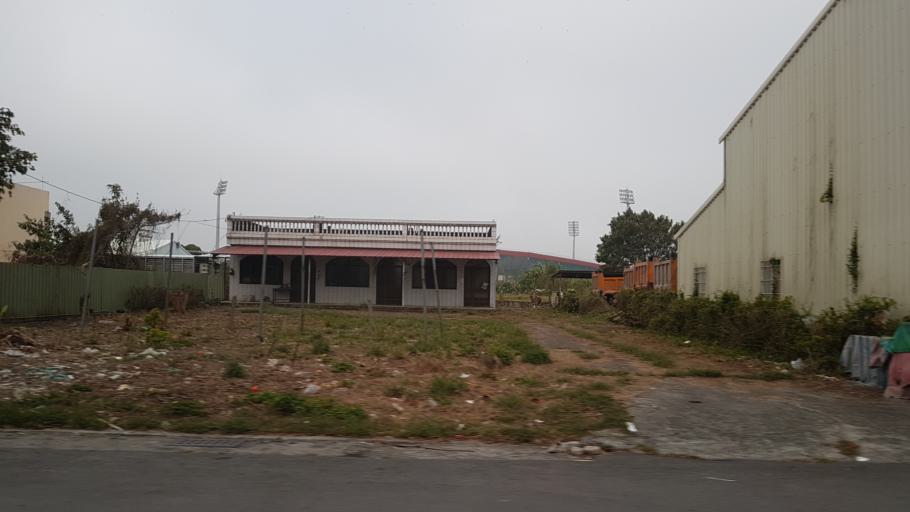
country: TW
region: Taiwan
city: Xinying
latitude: 23.3210
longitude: 120.3162
